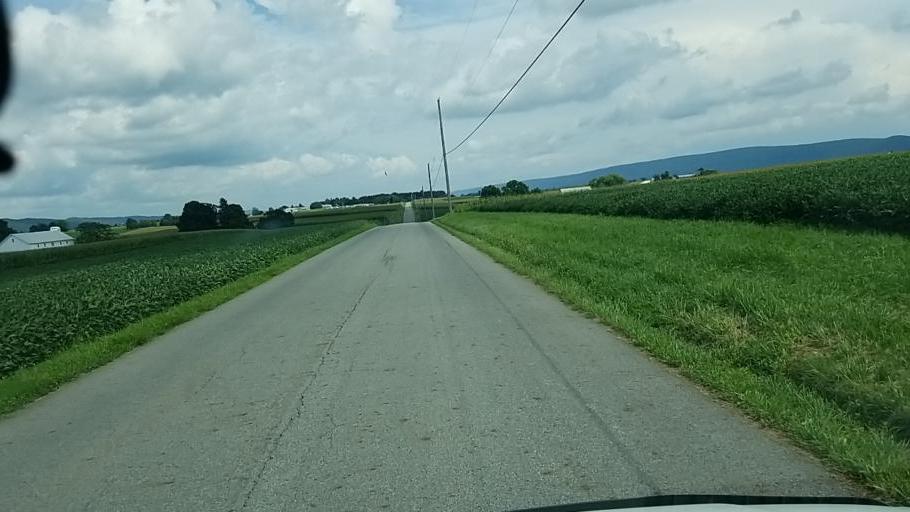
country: US
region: Pennsylvania
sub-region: Dauphin County
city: Elizabethville
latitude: 40.6126
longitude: -76.8263
